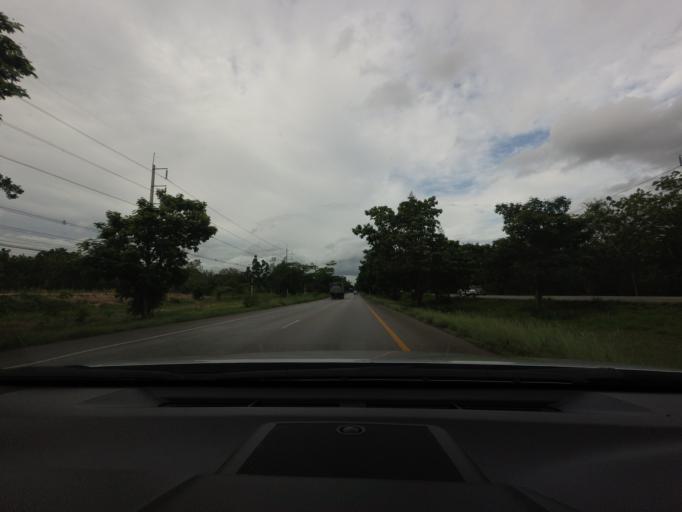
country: TH
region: Phetchaburi
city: Cha-am
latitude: 12.7007
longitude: 99.9076
